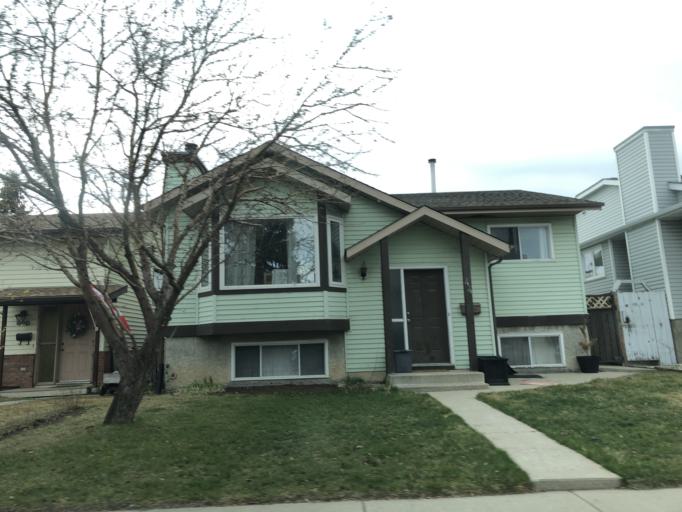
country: CA
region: Alberta
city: Calgary
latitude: 51.0717
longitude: -114.0110
